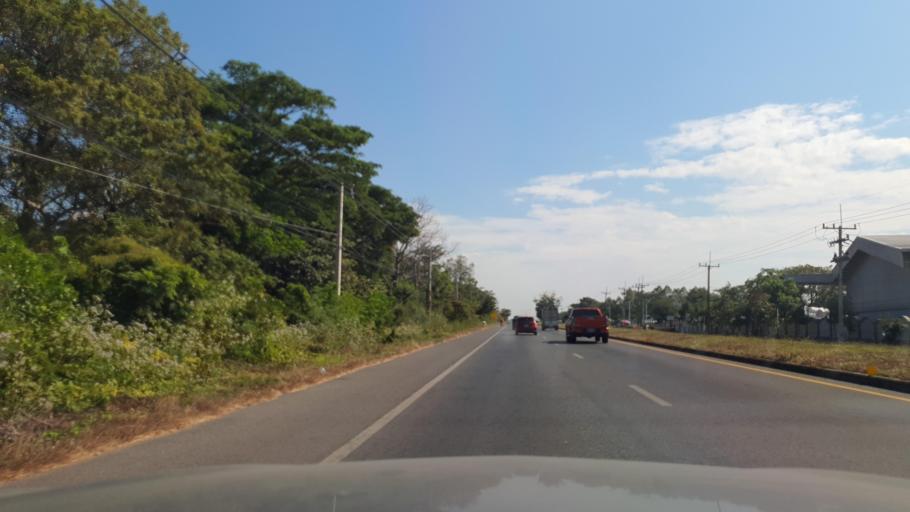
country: TH
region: Maha Sarakham
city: Chiang Yuen
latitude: 16.3738
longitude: 103.1517
